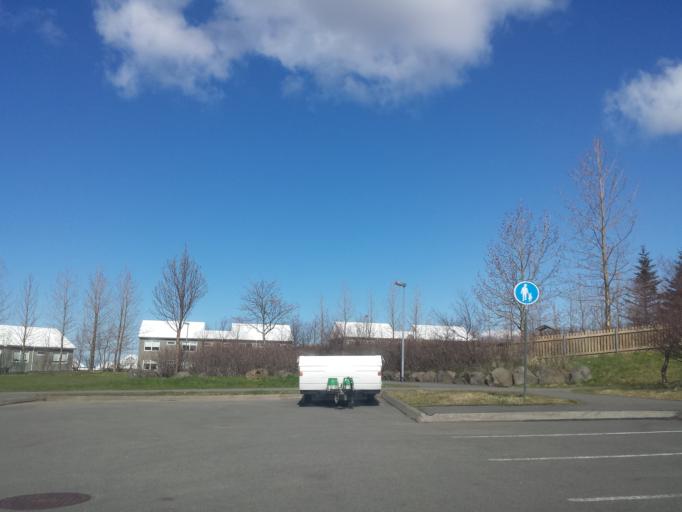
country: IS
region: Capital Region
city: Reykjavik
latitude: 64.0960
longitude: -21.8593
